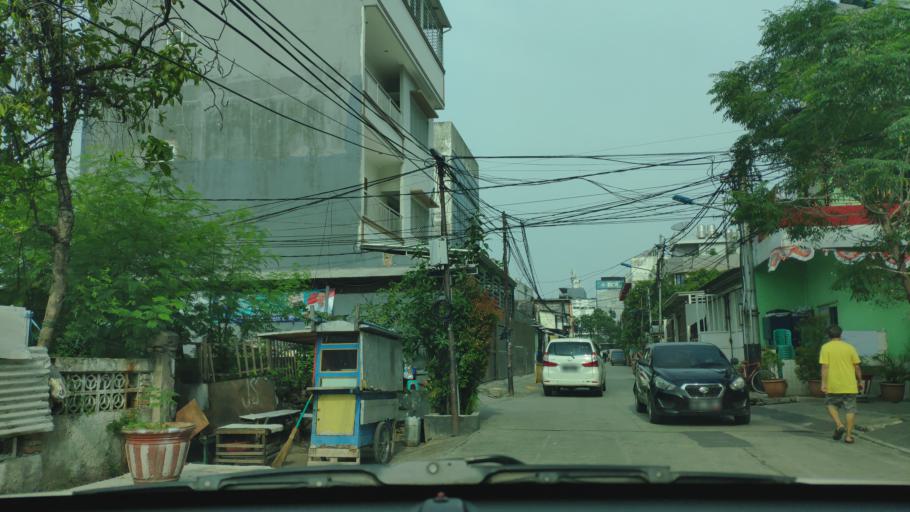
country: ID
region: Jakarta Raya
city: Jakarta
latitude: -6.1586
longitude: 106.8173
